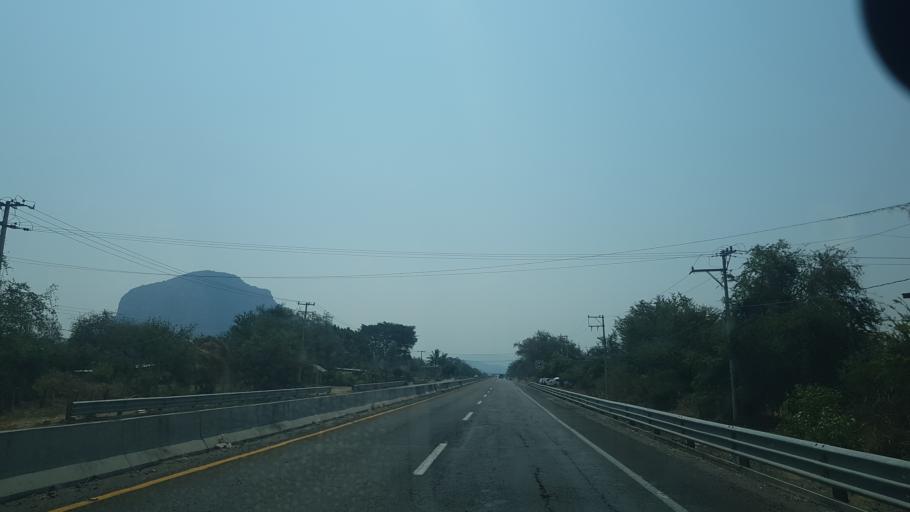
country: MX
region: Morelos
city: Jantetelco
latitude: 18.7122
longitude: -98.7829
